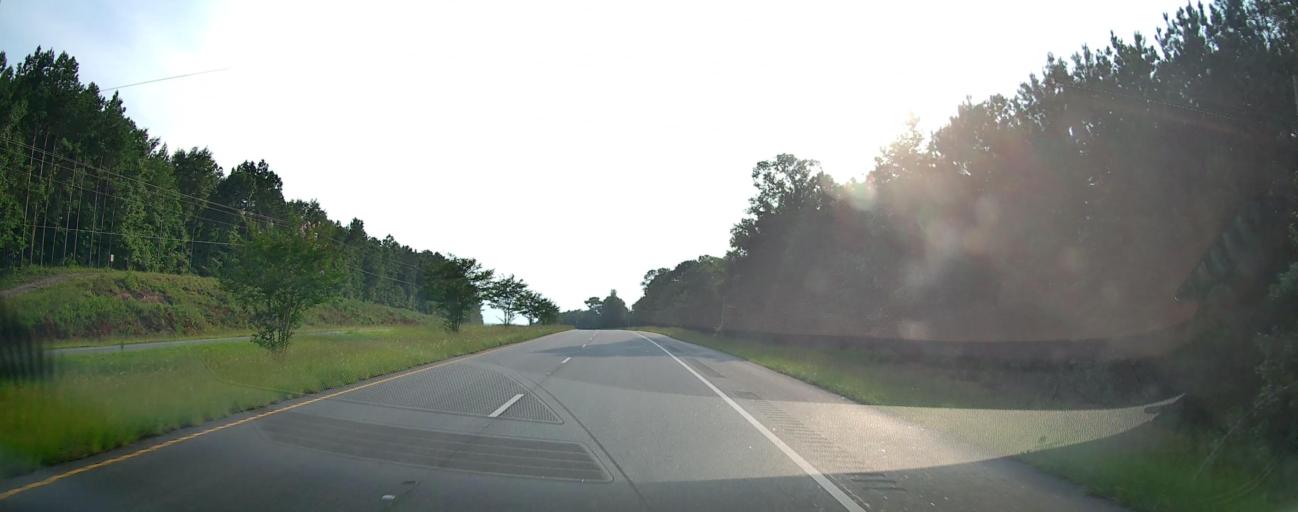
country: US
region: Georgia
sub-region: Talbot County
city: Talbotton
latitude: 32.5495
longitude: -84.6996
